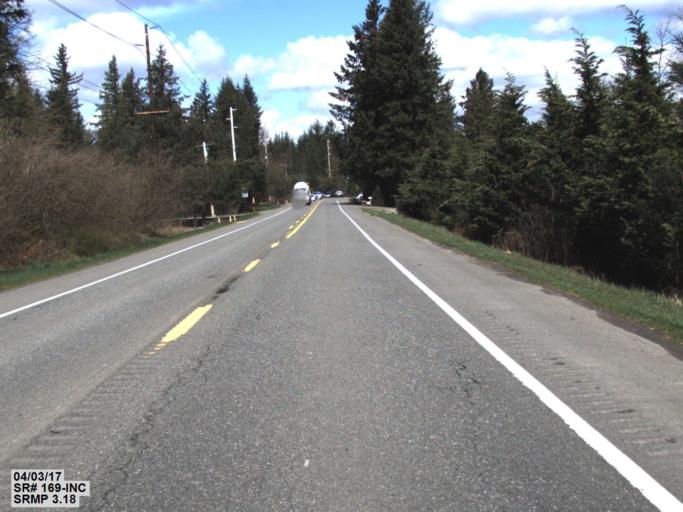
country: US
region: Washington
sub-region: King County
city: Enumclaw
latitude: 47.2502
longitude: -121.9900
